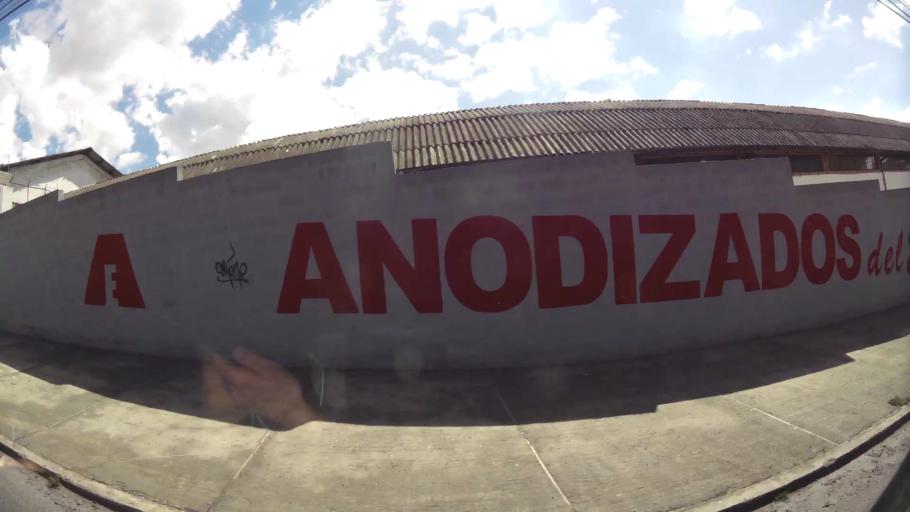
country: EC
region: Pichincha
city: Quito
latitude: -0.1143
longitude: -78.4747
